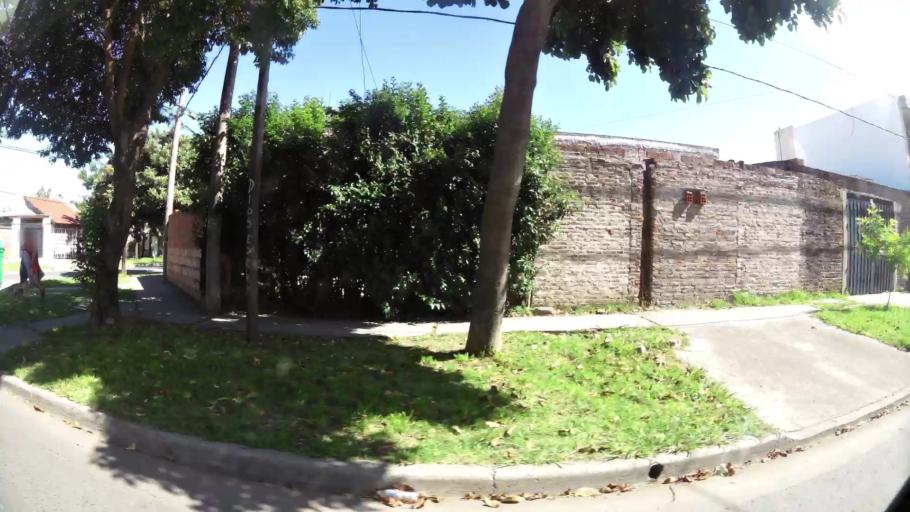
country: AR
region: Santa Fe
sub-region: Departamento de Rosario
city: Rosario
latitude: -32.9357
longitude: -60.7107
